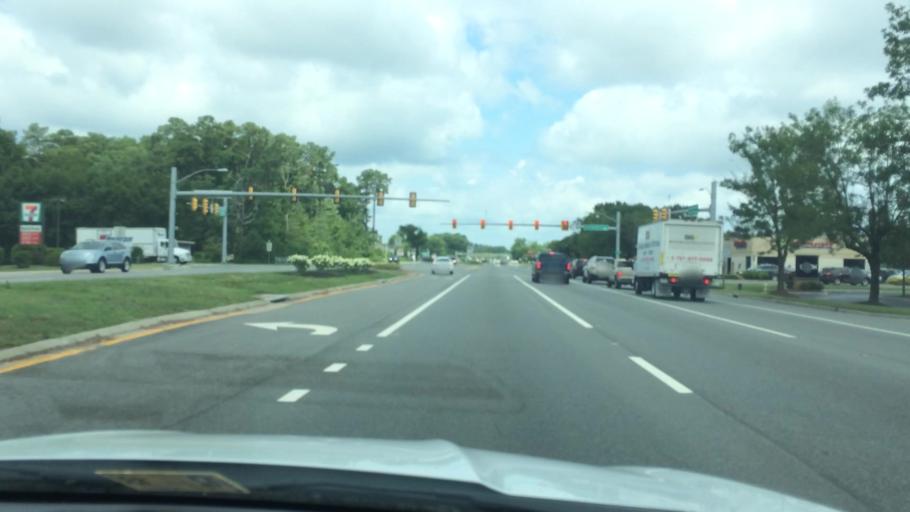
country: US
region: Virginia
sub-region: York County
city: Yorktown
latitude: 37.1549
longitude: -76.4616
